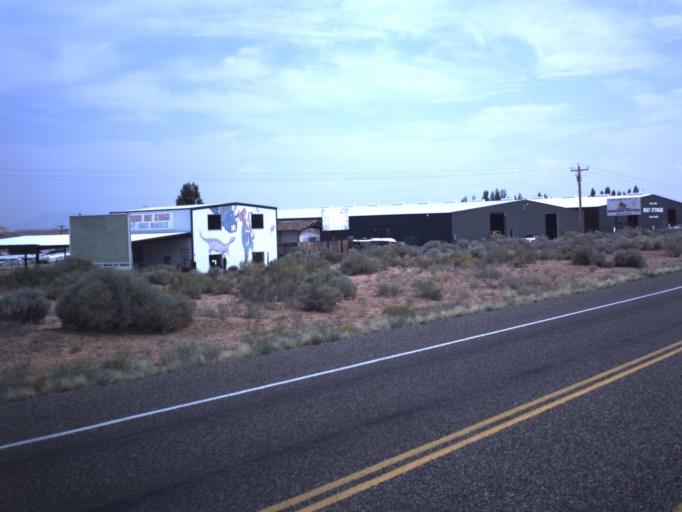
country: US
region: Arizona
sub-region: Coconino County
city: Page
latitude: 37.0655
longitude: -111.6462
